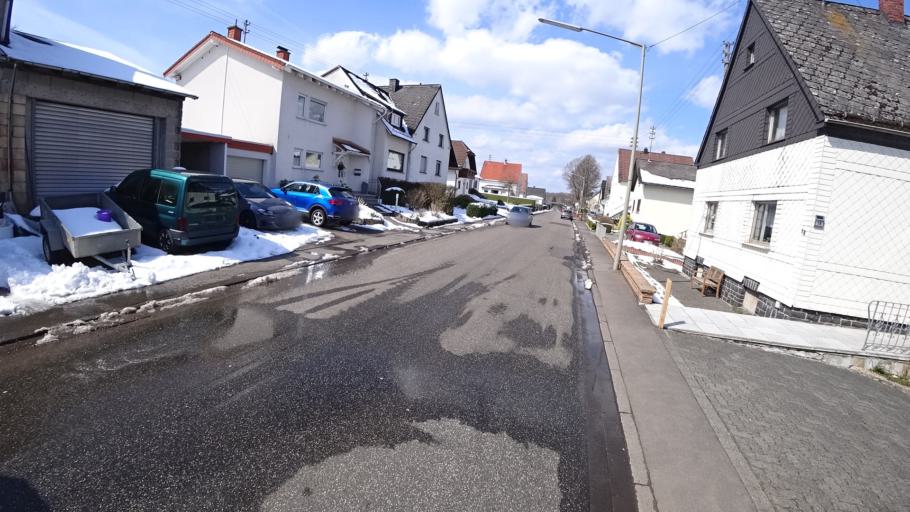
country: DE
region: Rheinland-Pfalz
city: Elkenroth
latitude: 50.7299
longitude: 7.8802
